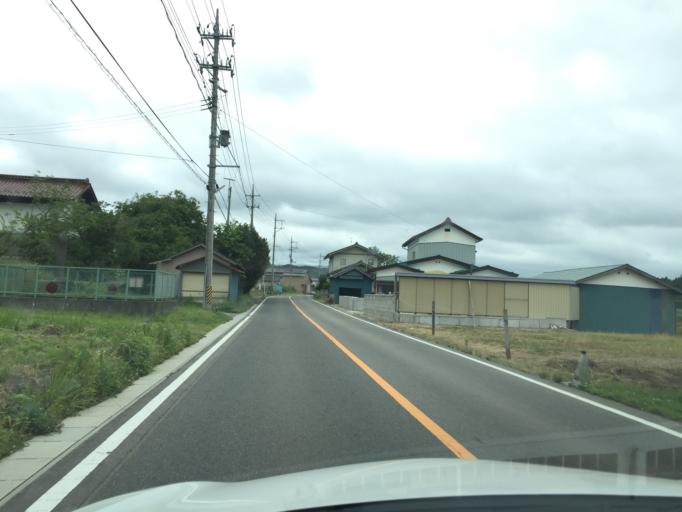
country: JP
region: Fukushima
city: Funehikimachi-funehiki
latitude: 37.4291
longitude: 140.5941
